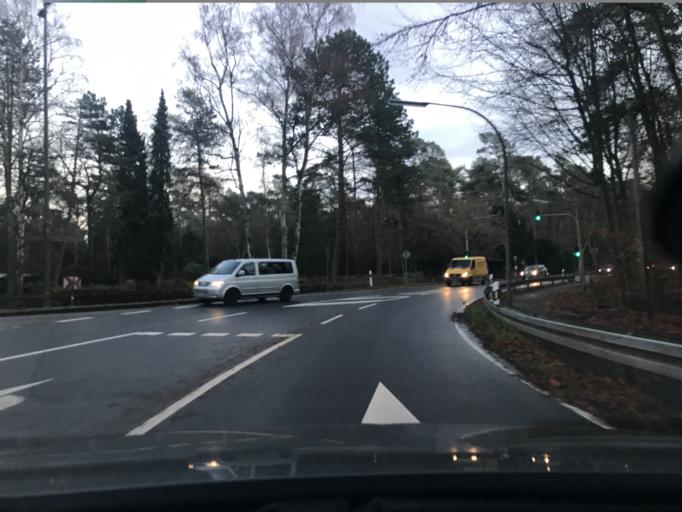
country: DE
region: North Rhine-Westphalia
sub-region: Regierungsbezirk Koln
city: Merheim
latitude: 50.9648
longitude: 7.0721
